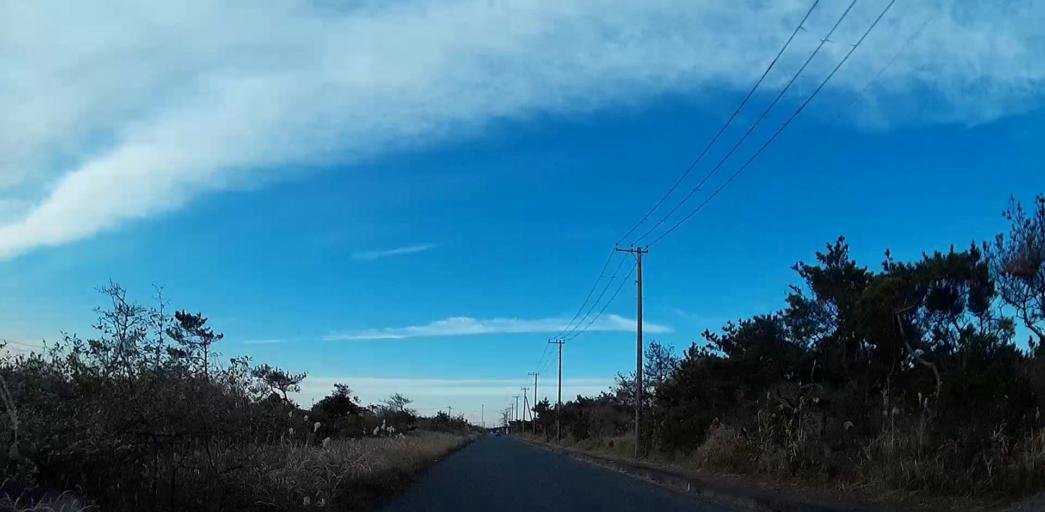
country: JP
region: Chiba
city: Hasaki
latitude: 35.8023
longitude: 140.7886
